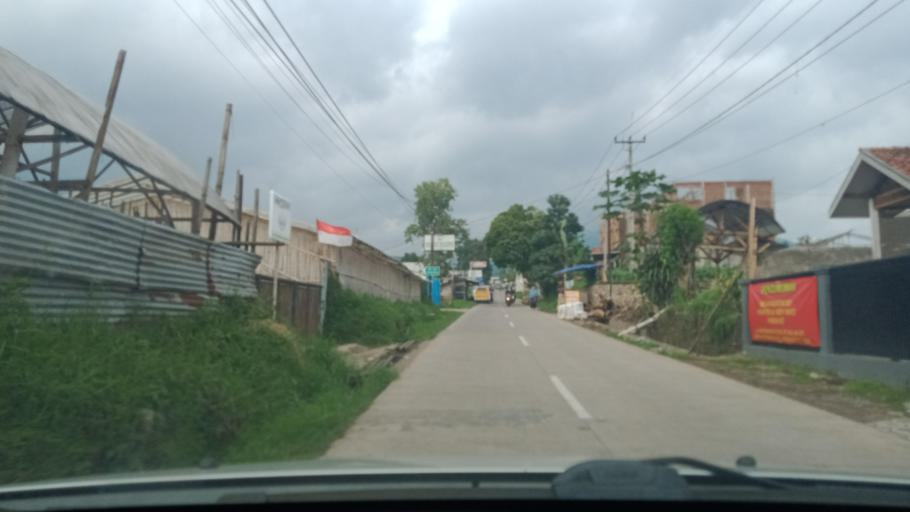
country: ID
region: West Java
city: Lembang
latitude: -6.8110
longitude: 107.5769
